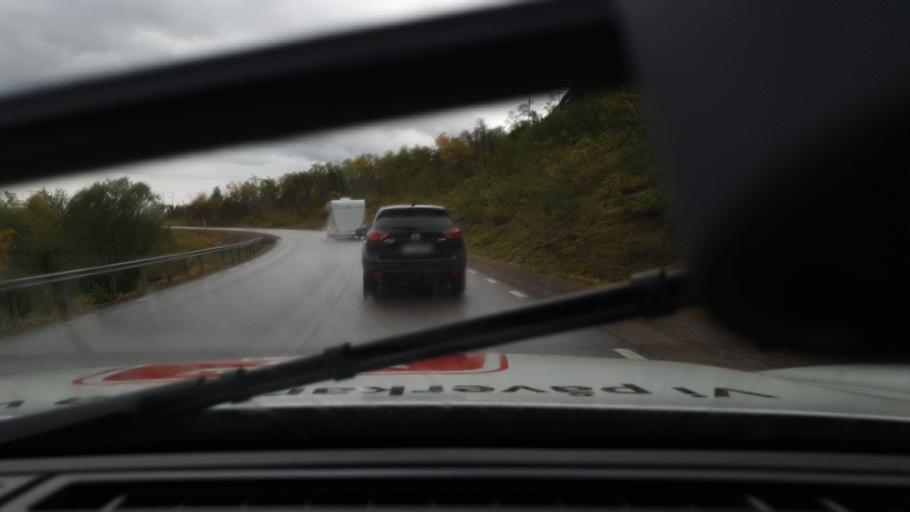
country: NO
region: Troms
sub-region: Bardu
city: Setermoen
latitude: 68.4261
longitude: 18.4212
